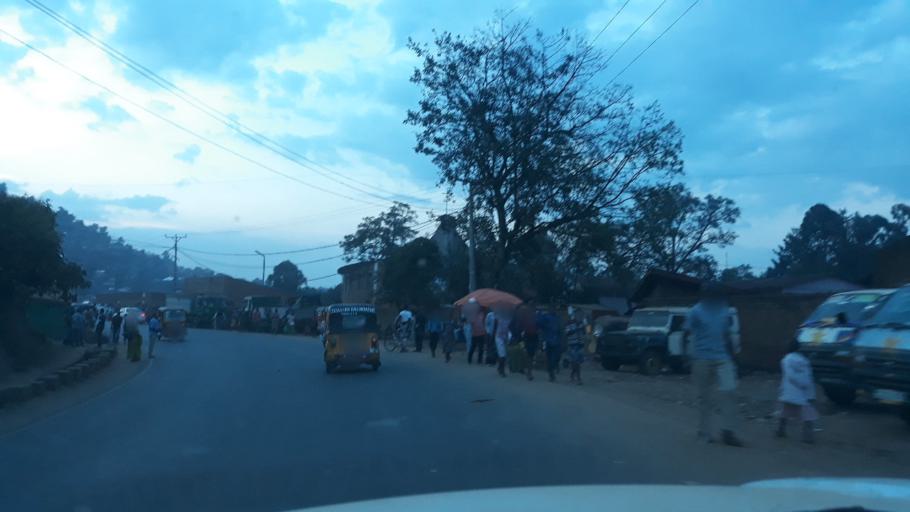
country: CD
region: South Kivu
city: Bukavu
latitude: -2.5343
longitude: 28.8577
